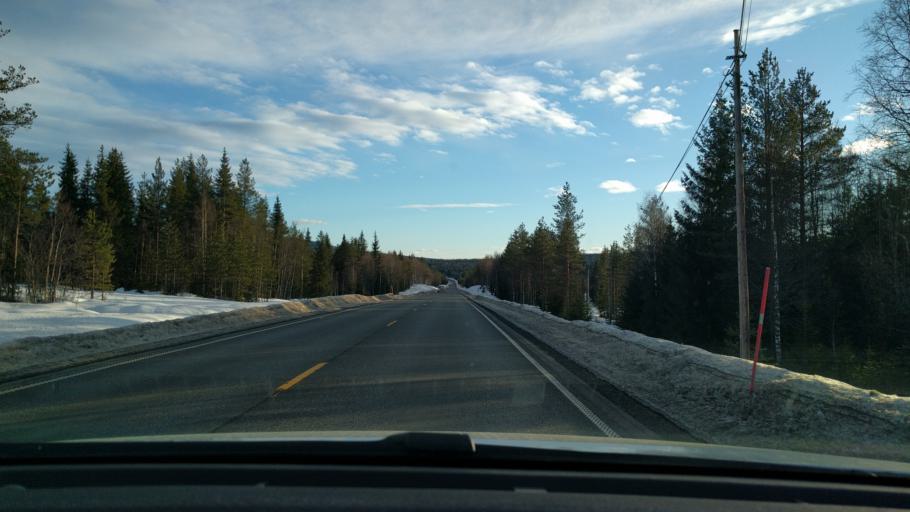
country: NO
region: Hedmark
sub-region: Elverum
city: Elverum
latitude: 61.0399
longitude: 11.8715
